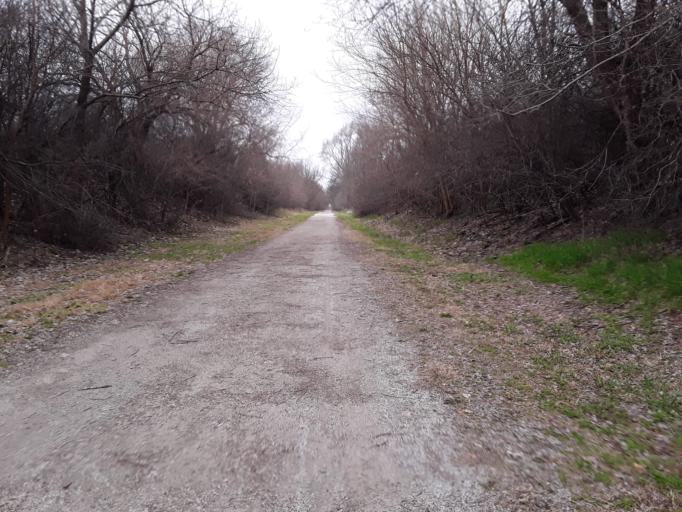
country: US
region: Nebraska
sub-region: Lancaster County
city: Lincoln
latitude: 40.8513
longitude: -96.6093
